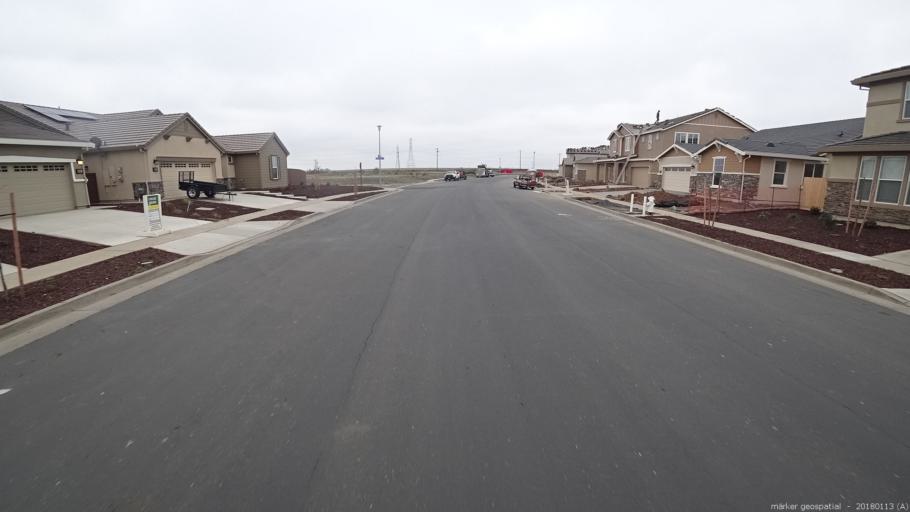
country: US
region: California
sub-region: Sacramento County
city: Gold River
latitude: 38.5706
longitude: -121.1971
